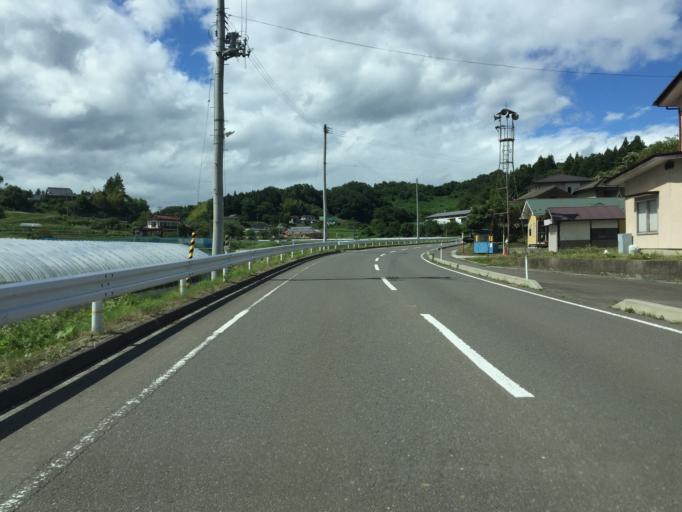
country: JP
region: Fukushima
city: Fukushima-shi
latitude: 37.6673
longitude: 140.5398
